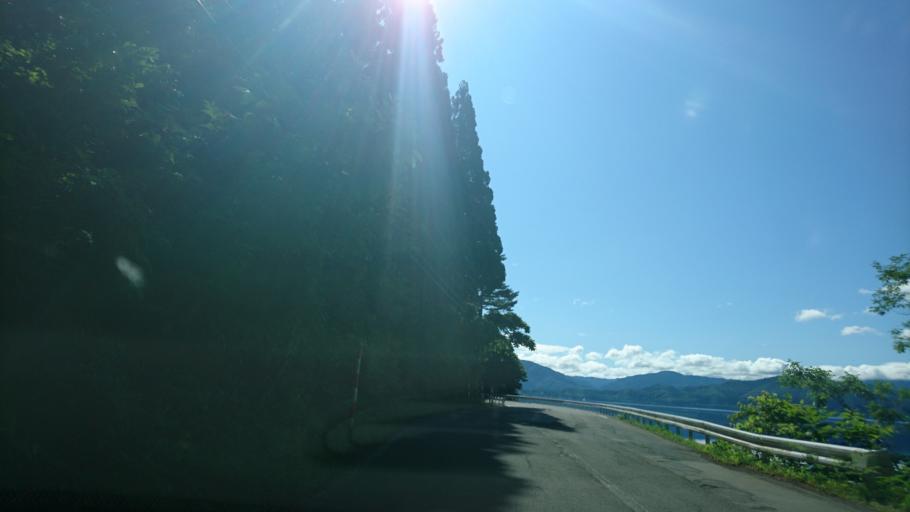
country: JP
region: Akita
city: Kakunodatemachi
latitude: 39.7514
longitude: 140.6521
